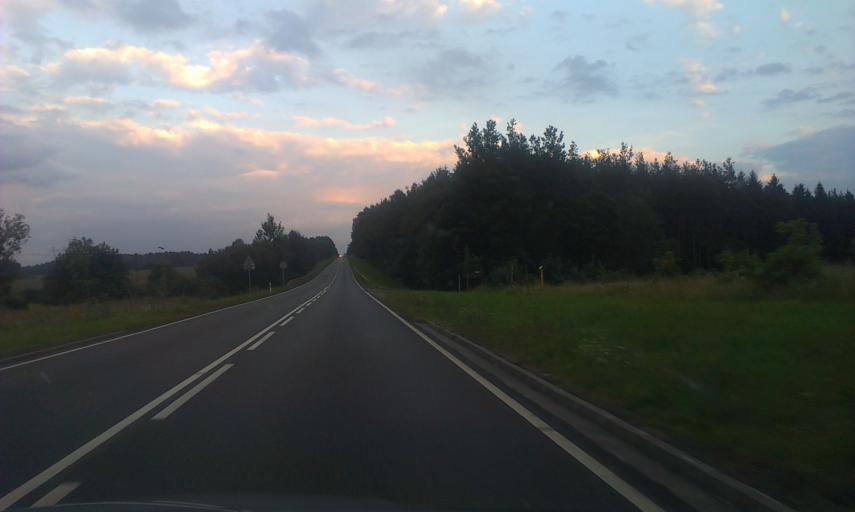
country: PL
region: West Pomeranian Voivodeship
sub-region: Powiat koszalinski
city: Sianow
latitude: 54.1201
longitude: 16.3118
